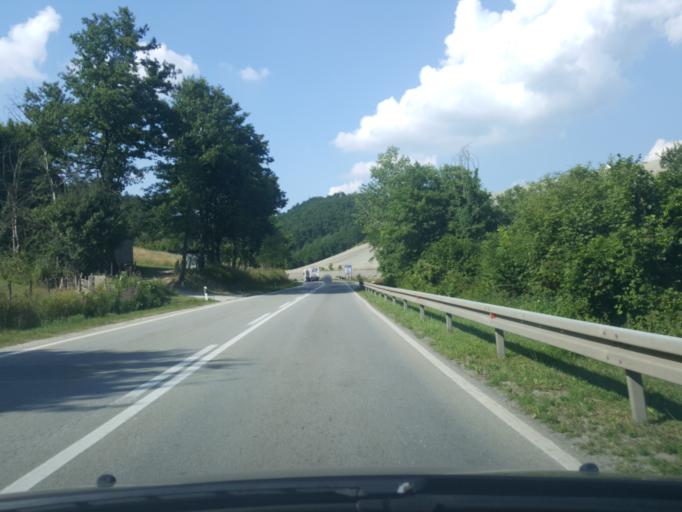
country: RS
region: Central Serbia
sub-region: Moravicki Okrug
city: Gornji Milanovac
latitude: 44.1036
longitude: 20.4823
